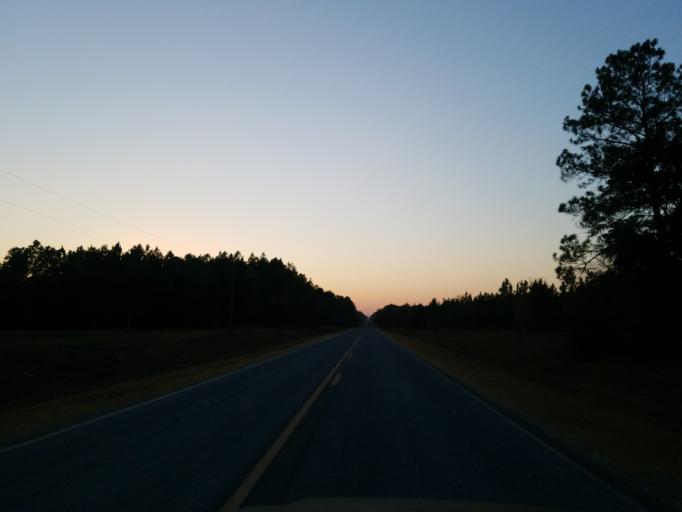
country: US
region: Georgia
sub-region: Ben Hill County
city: Fitzgerald
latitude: 31.7209
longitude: -83.4393
